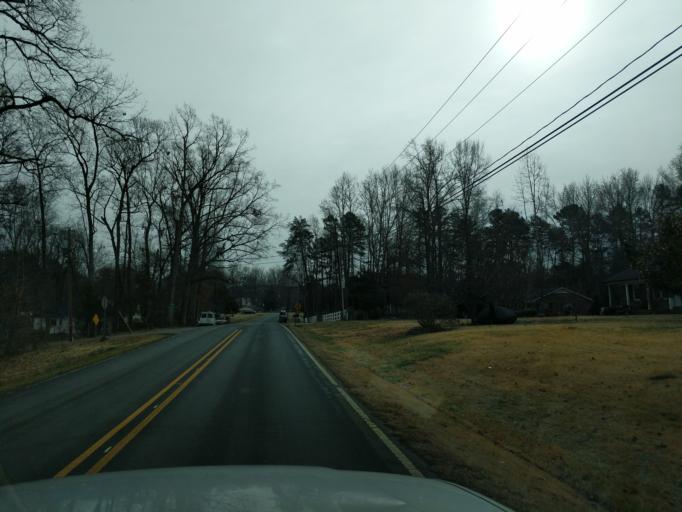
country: US
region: North Carolina
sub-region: Mecklenburg County
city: Charlotte
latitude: 35.3184
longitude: -80.8887
